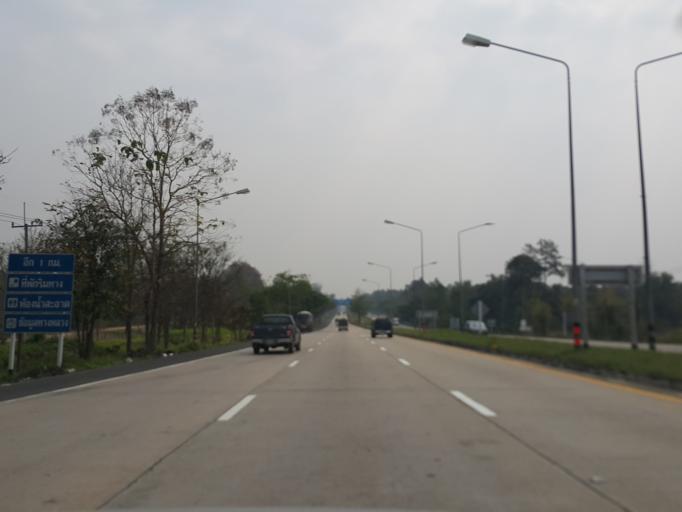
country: TH
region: Lampang
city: Hang Chat
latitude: 18.3249
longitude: 99.2898
